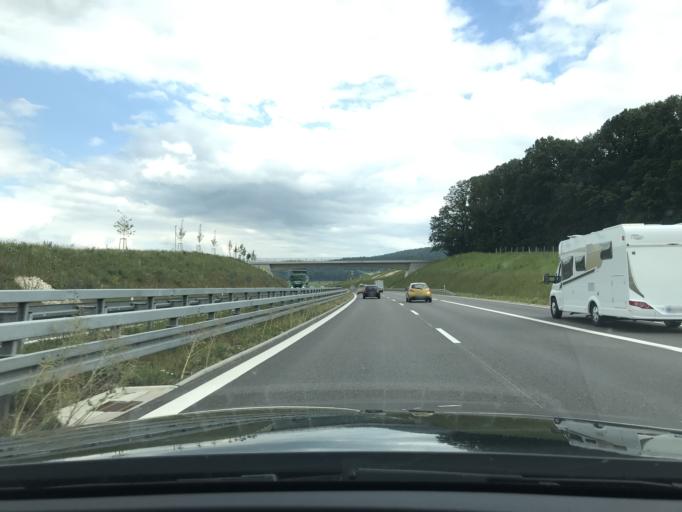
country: DE
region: Baden-Wuerttemberg
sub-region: Regierungsbezirk Stuttgart
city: Mogglingen
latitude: 48.8132
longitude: 9.9563
